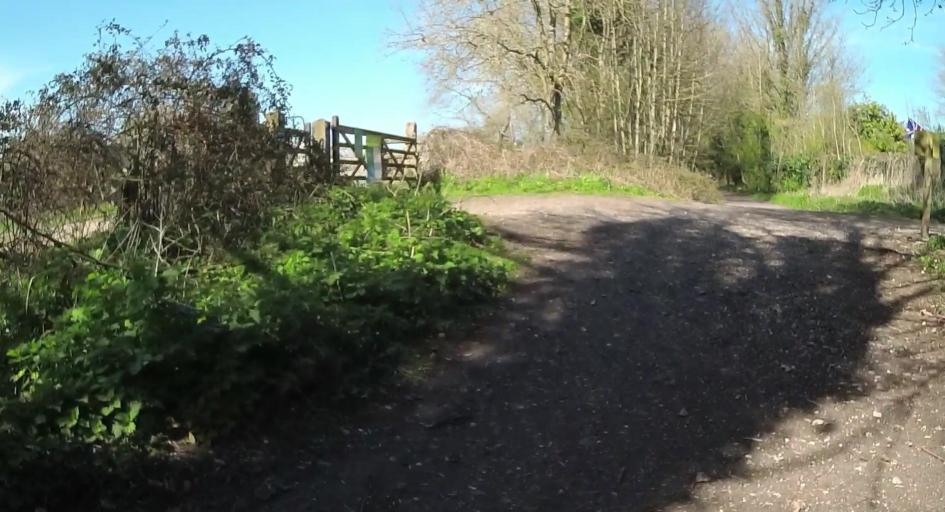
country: GB
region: England
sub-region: Hampshire
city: Abbotts Ann
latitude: 51.1101
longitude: -1.4914
